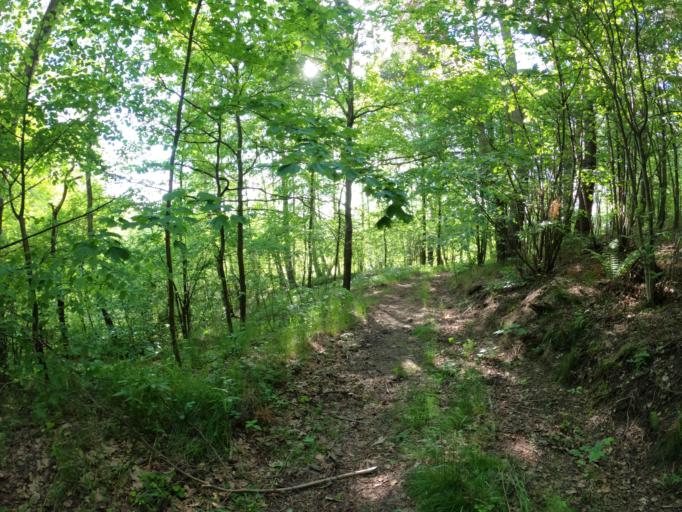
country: PL
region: Warmian-Masurian Voivodeship
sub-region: Powiat lidzbarski
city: Lidzbark Warminski
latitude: 54.1267
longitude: 20.6087
